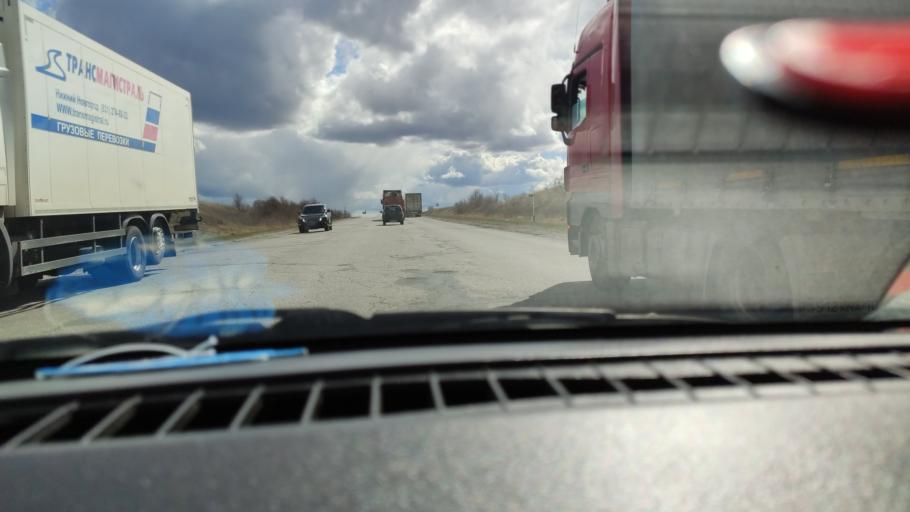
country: RU
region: Samara
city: Varlamovo
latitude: 53.0877
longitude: 48.3550
